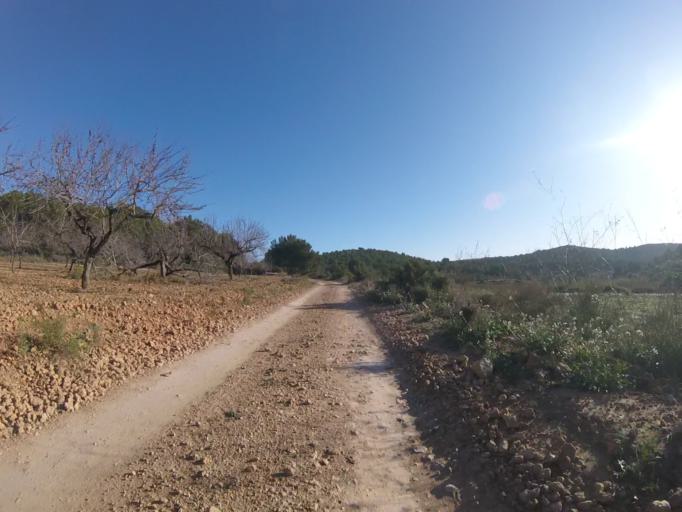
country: ES
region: Valencia
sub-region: Provincia de Castello
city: Torreblanca
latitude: 40.2520
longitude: 0.1862
